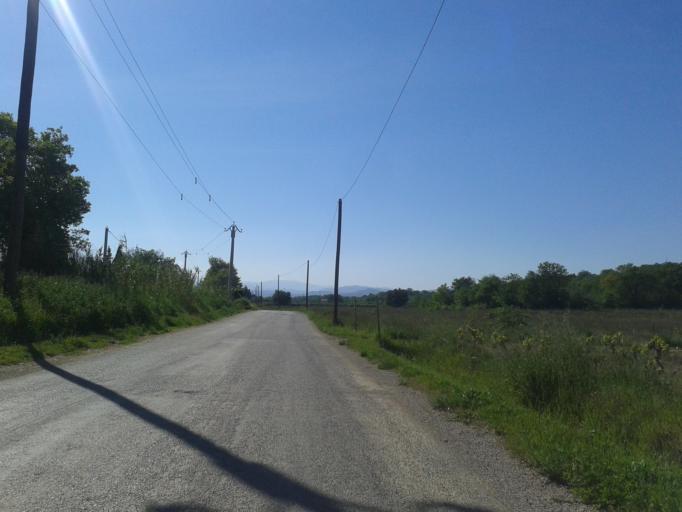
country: FR
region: Languedoc-Roussillon
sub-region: Departement des Pyrenees-Orientales
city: Pezilla-la-Riviere
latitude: 42.7005
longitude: 2.7583
